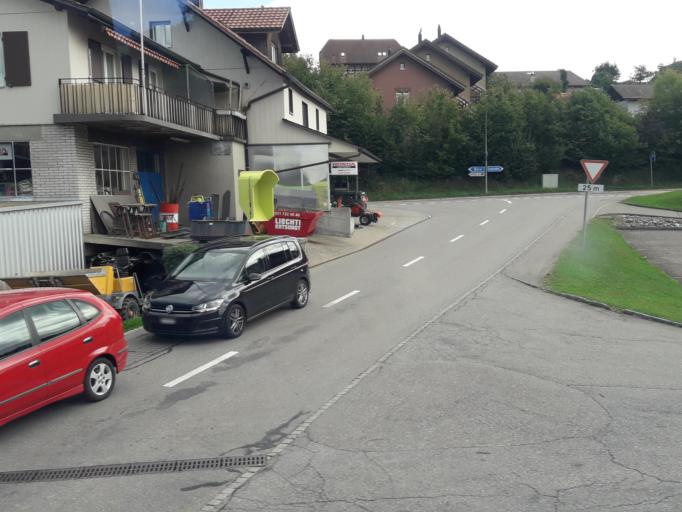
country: CH
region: Bern
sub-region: Bern-Mittelland District
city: Wahlern
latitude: 46.8425
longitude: 7.3475
